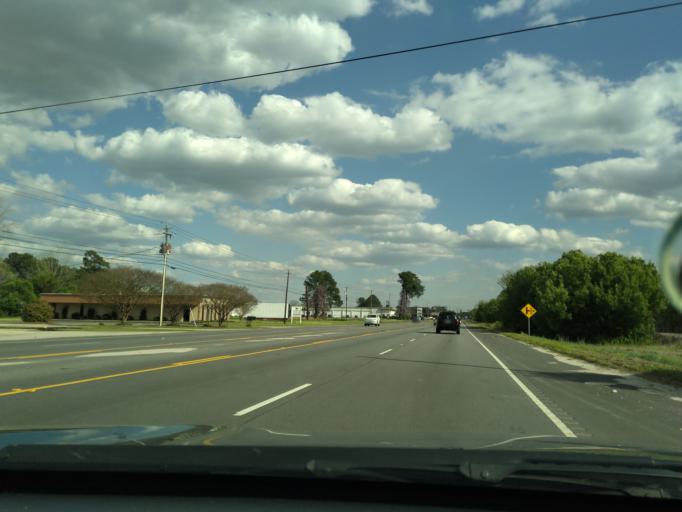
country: US
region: South Carolina
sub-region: Florence County
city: Florence
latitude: 34.2152
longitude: -79.7814
